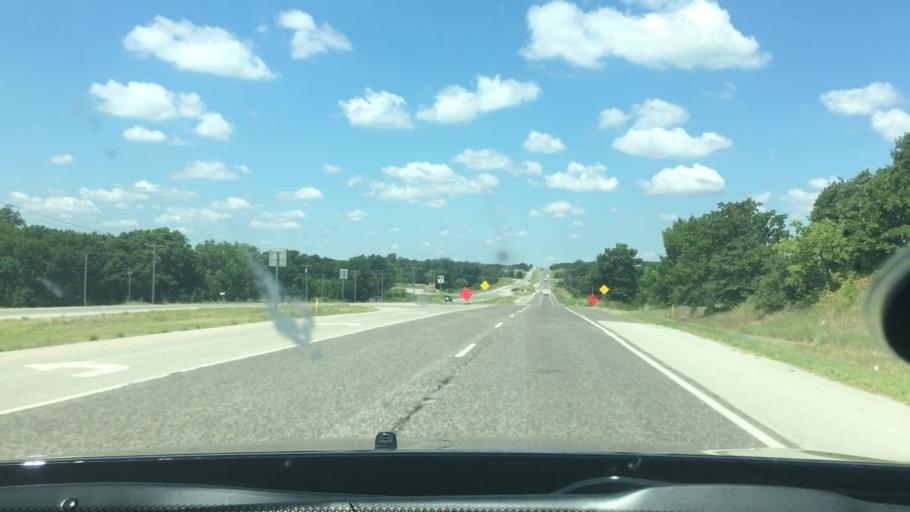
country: US
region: Oklahoma
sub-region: Carter County
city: Lone Grove
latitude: 34.1731
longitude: -97.3079
